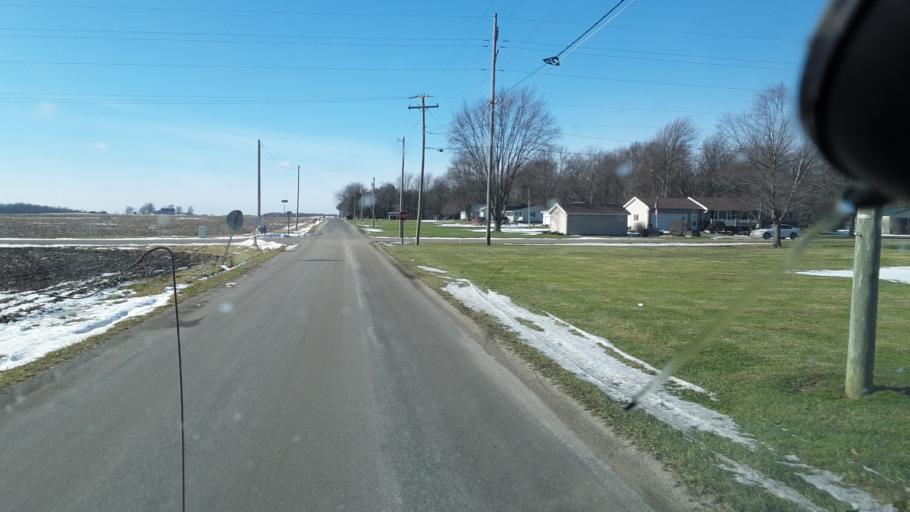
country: US
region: Ohio
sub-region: Huron County
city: Plymouth
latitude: 40.9448
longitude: -82.6852
